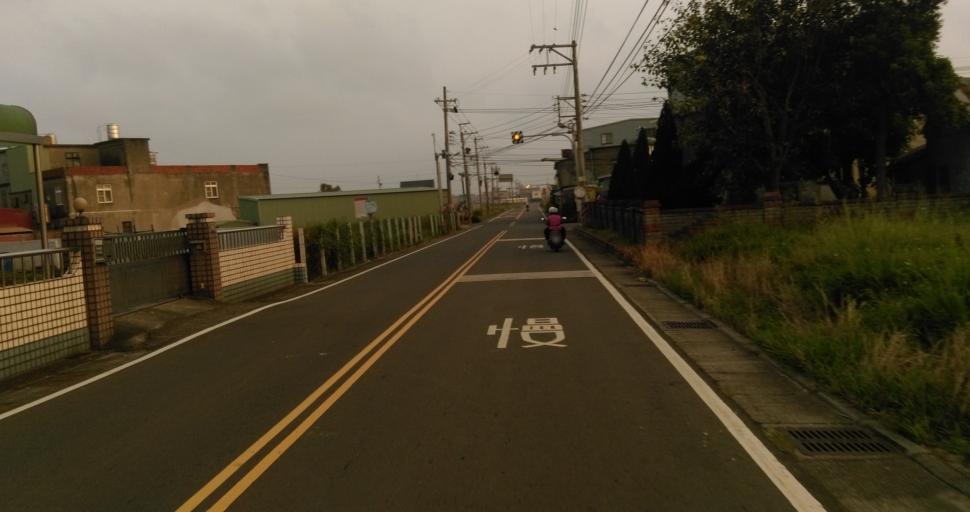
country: TW
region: Taiwan
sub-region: Hsinchu
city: Zhubei
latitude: 24.8742
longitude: 120.9560
